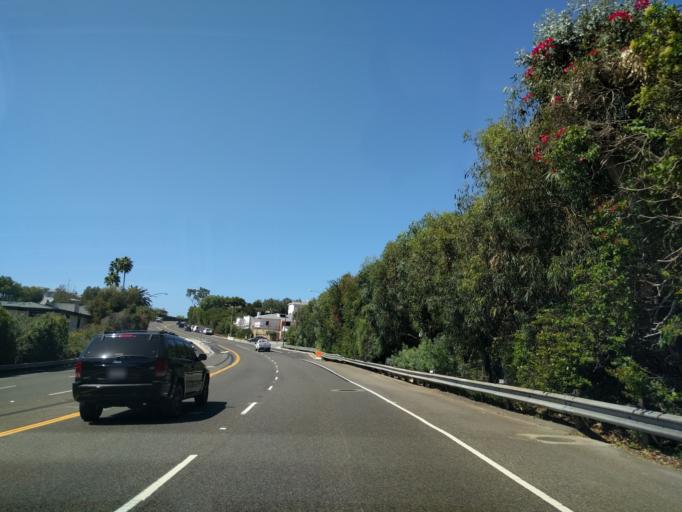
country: US
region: California
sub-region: Orange County
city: Laguna Beach
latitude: 33.5528
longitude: -117.8069
